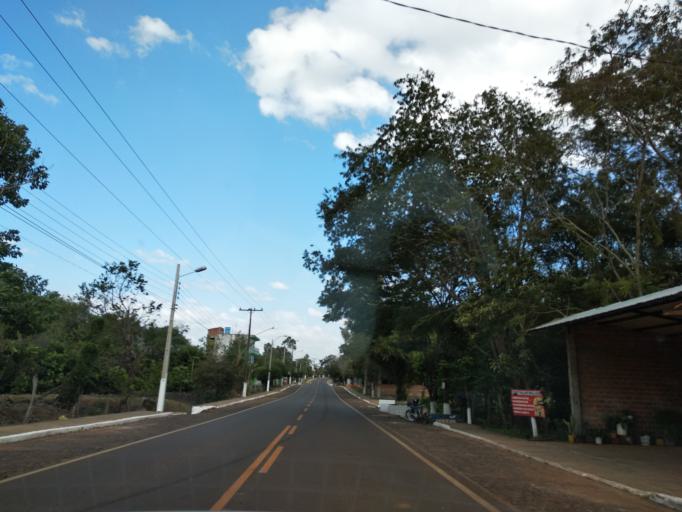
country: PY
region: Itapua
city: San Juan del Parana
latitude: -27.2992
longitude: -55.9649
